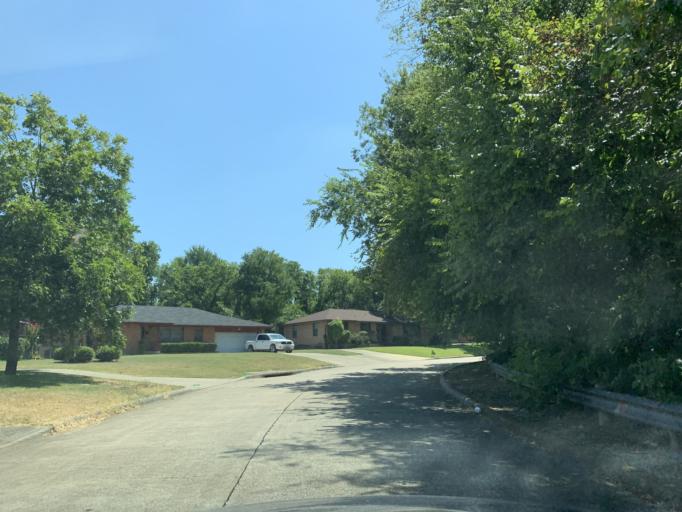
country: US
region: Texas
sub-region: Dallas County
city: Cockrell Hill
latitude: 32.6782
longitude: -96.8094
